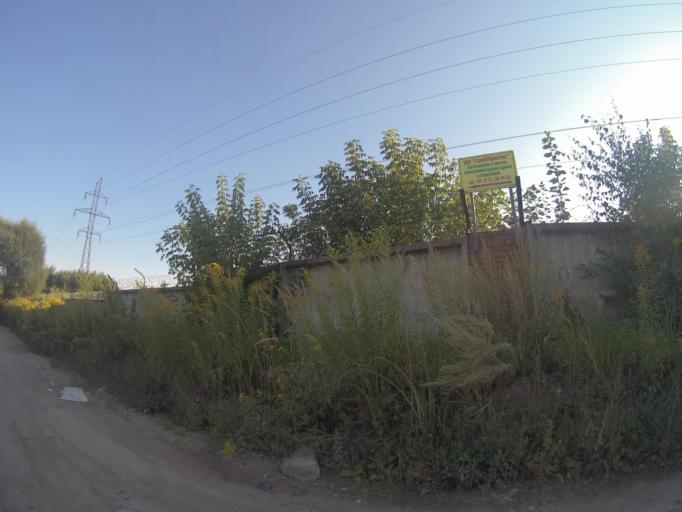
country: RU
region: Vladimir
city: Kommunar
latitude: 56.1390
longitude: 40.4585
